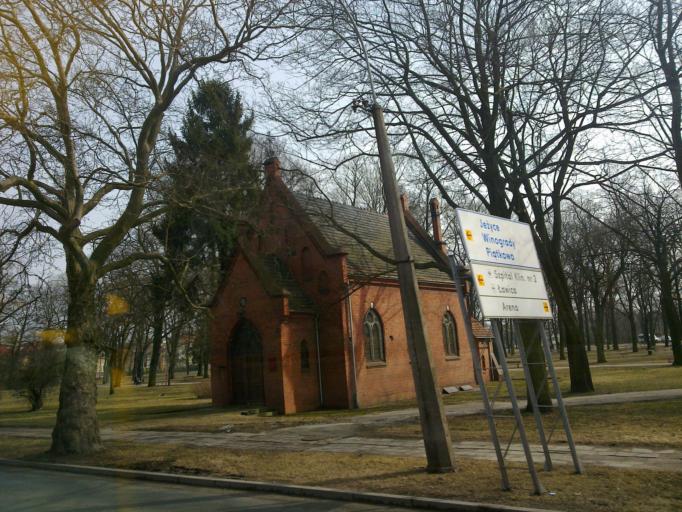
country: PL
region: Greater Poland Voivodeship
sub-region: Poznan
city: Poznan
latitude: 52.4017
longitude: 16.8865
